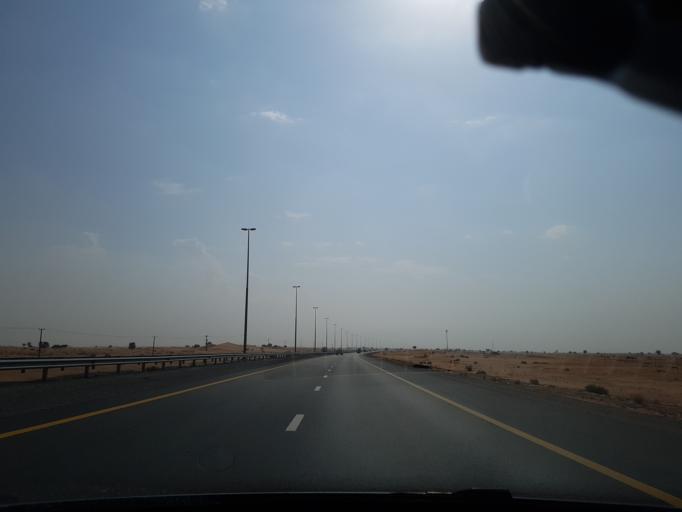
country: AE
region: Umm al Qaywayn
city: Umm al Qaywayn
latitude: 25.5425
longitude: 55.7785
